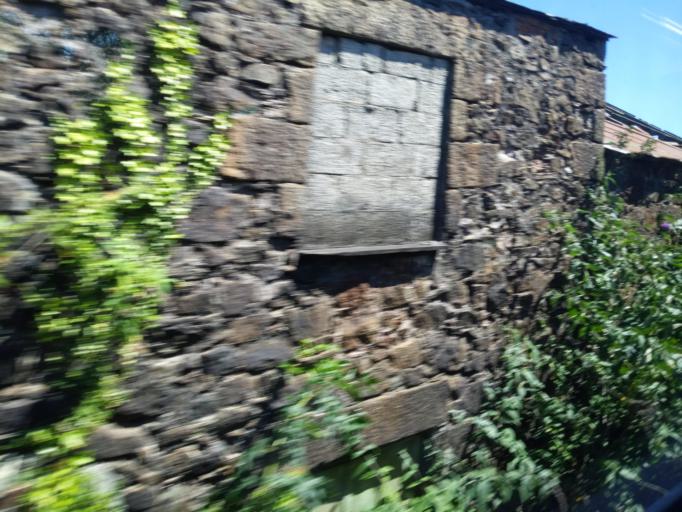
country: GB
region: England
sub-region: Cornwall
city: Redruth
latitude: 50.2372
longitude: -5.2251
